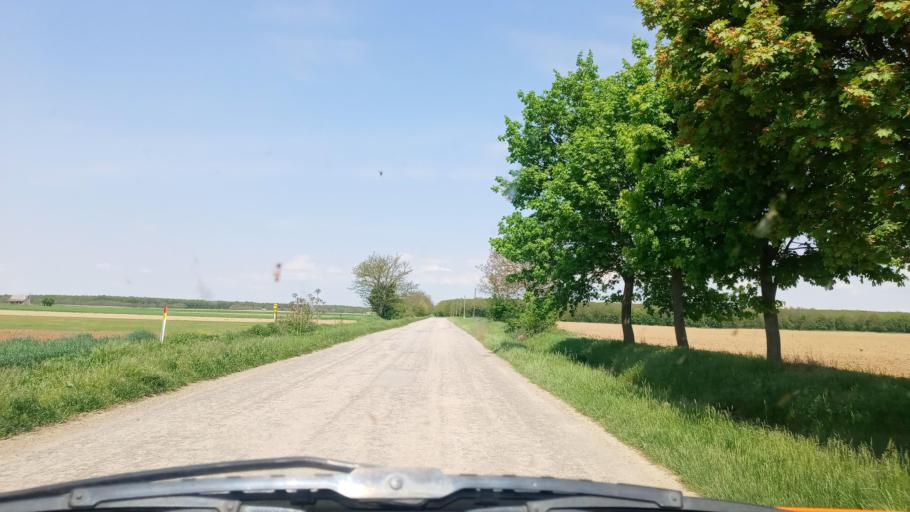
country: HU
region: Baranya
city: Boly
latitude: 45.8777
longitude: 18.5771
